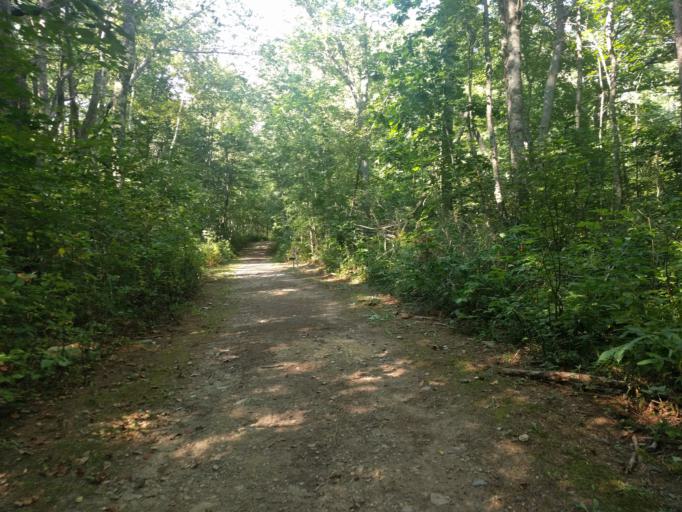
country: US
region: Maine
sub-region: Waldo County
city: Belfast
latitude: 44.4320
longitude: -68.9466
